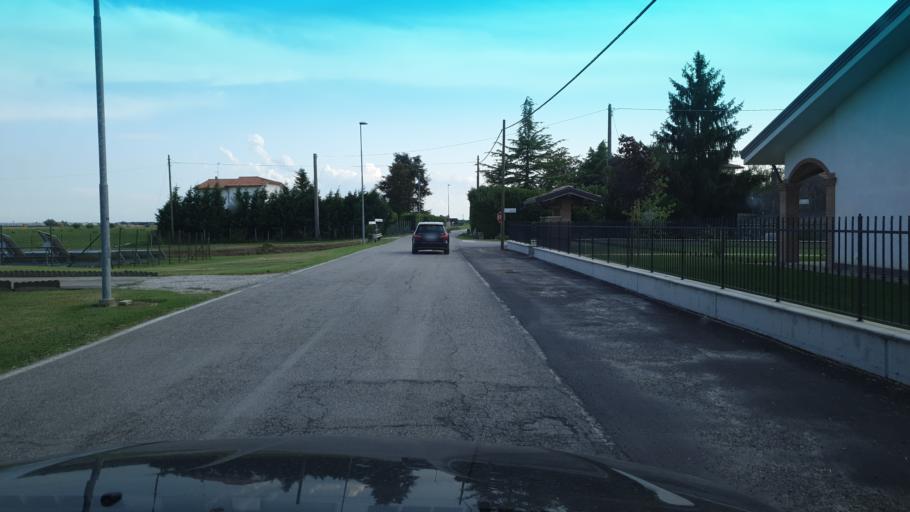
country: IT
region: Veneto
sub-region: Provincia di Rovigo
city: Castelguglielmo
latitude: 45.0191
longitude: 11.5349
